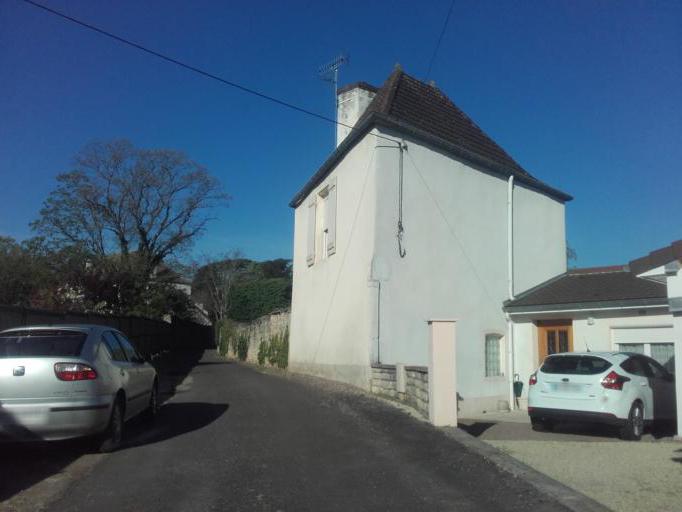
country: FR
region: Bourgogne
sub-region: Departement de Saone-et-Loire
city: Givry
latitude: 46.7804
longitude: 4.7446
